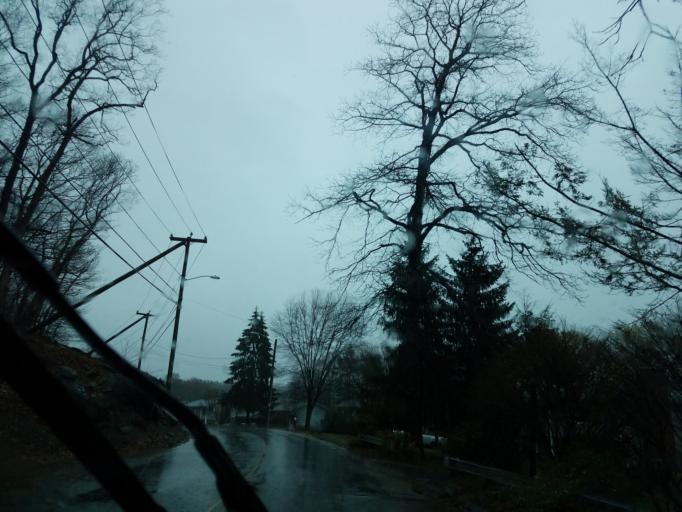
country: US
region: Connecticut
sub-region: New Haven County
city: Waterbury
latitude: 41.5374
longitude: -73.0781
